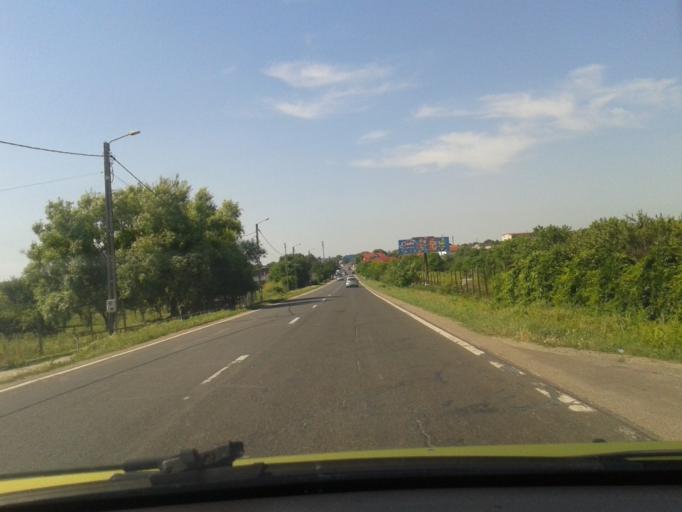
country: RO
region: Constanta
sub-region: Municipiul Mangalia
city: Mangalia
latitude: 43.7575
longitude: 28.5723
